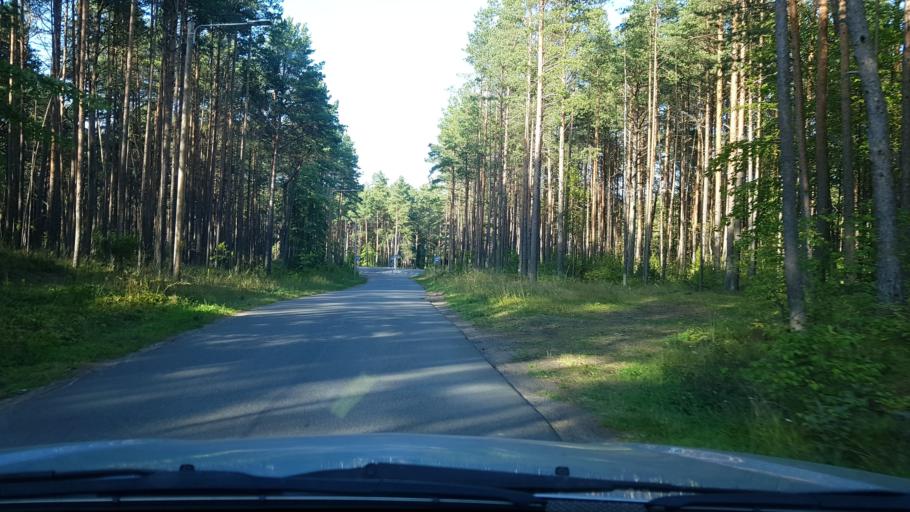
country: EE
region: Ida-Virumaa
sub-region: Narva-Joesuu linn
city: Narva-Joesuu
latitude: 59.4513
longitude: 28.0719
